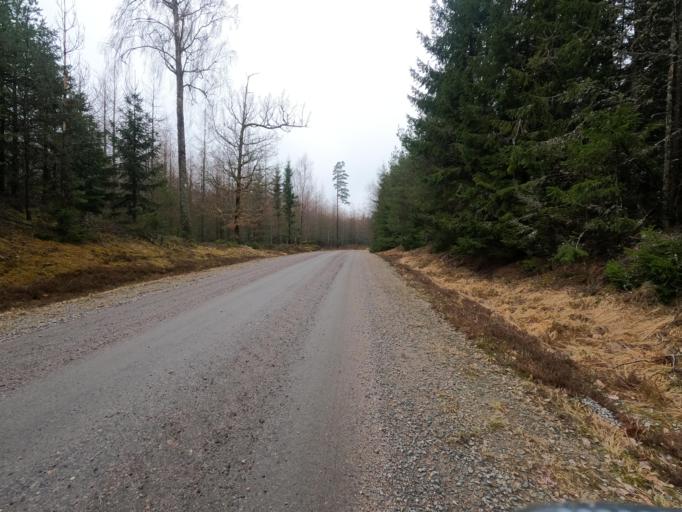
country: SE
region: Kronoberg
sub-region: Markaryds Kommun
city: Stromsnasbruk
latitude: 56.8115
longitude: 13.5687
